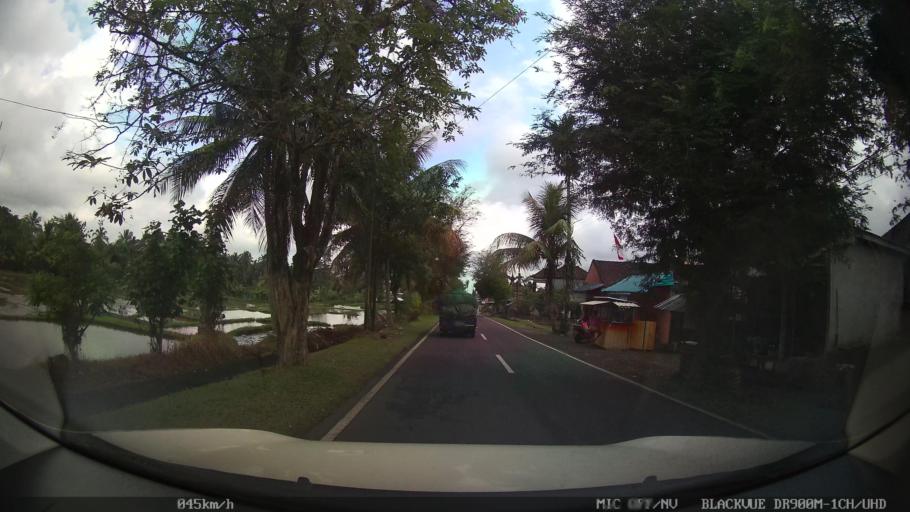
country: ID
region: Bali
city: Pohgending Kawan
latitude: -8.4400
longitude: 115.1419
